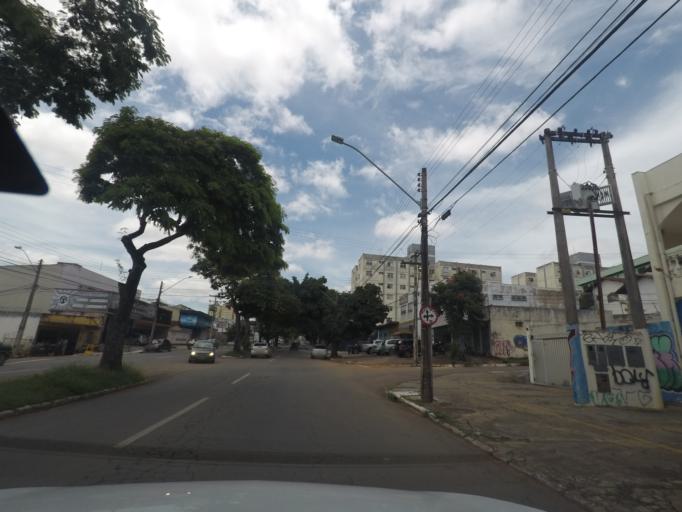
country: BR
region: Goias
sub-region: Goiania
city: Goiania
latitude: -16.6654
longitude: -49.2377
